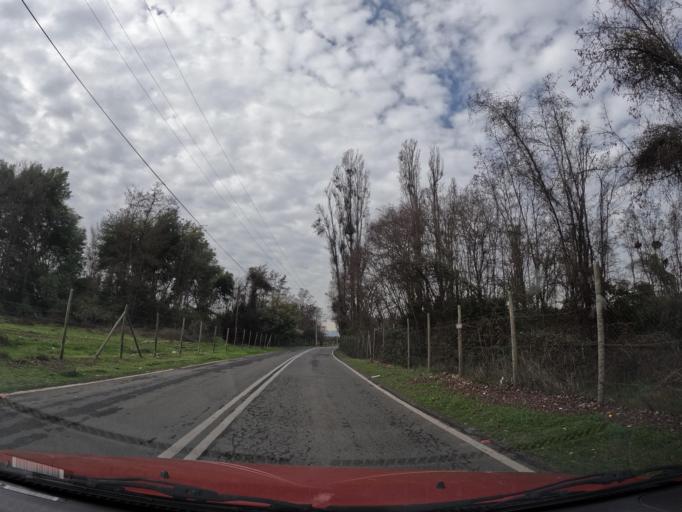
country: CL
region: Maule
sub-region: Provincia de Linares
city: Linares
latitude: -35.8661
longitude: -71.6258
